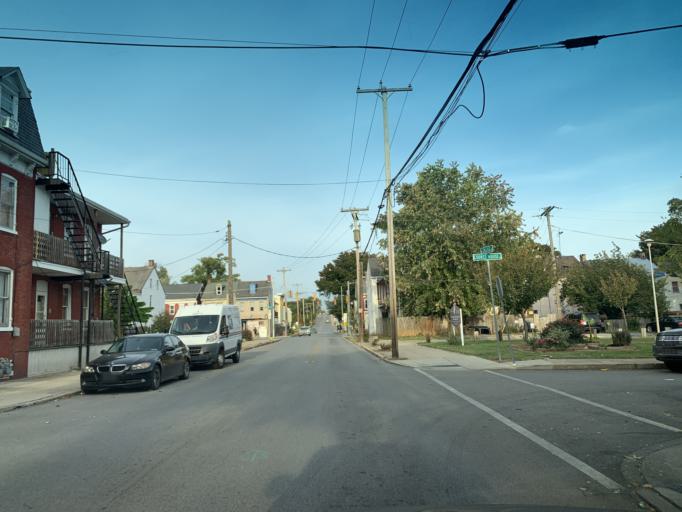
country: US
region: Pennsylvania
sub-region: York County
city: York
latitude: 39.9552
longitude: -76.7358
